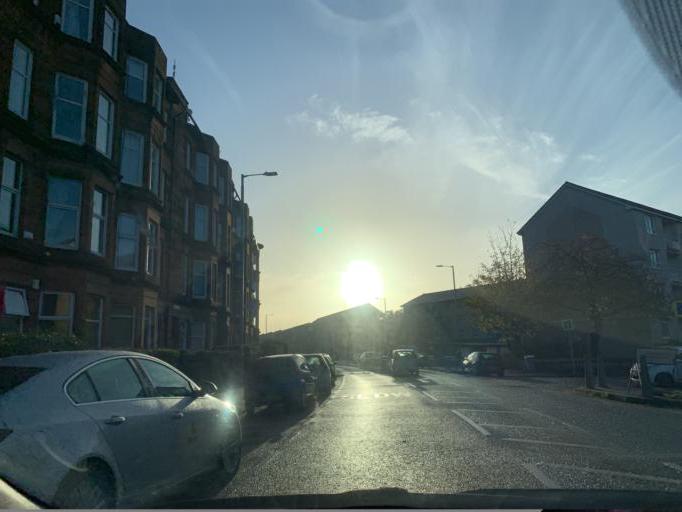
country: GB
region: Scotland
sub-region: East Renfrewshire
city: Giffnock
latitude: 55.8242
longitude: -4.2826
